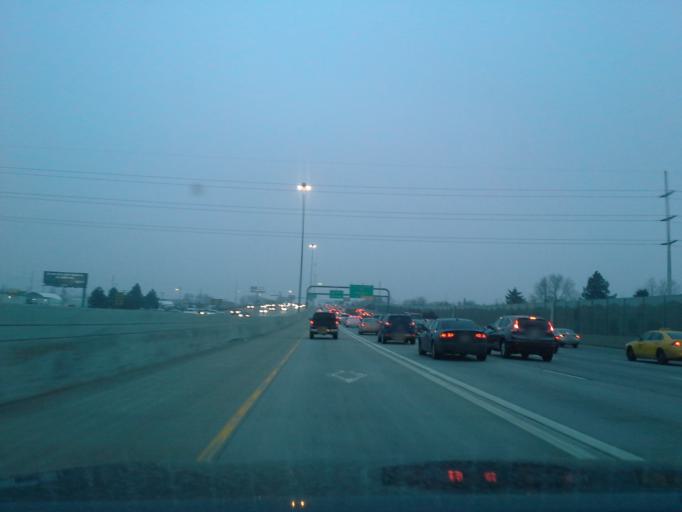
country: US
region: Utah
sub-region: Salt Lake County
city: Murray
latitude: 40.6483
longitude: -111.9024
